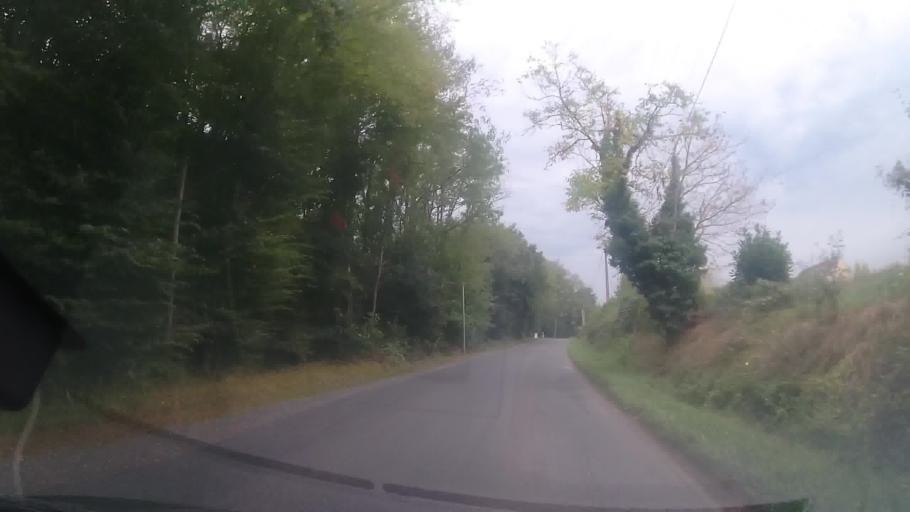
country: FR
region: Aquitaine
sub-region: Departement de la Dordogne
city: Carsac-Aillac
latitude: 44.8379
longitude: 1.2988
